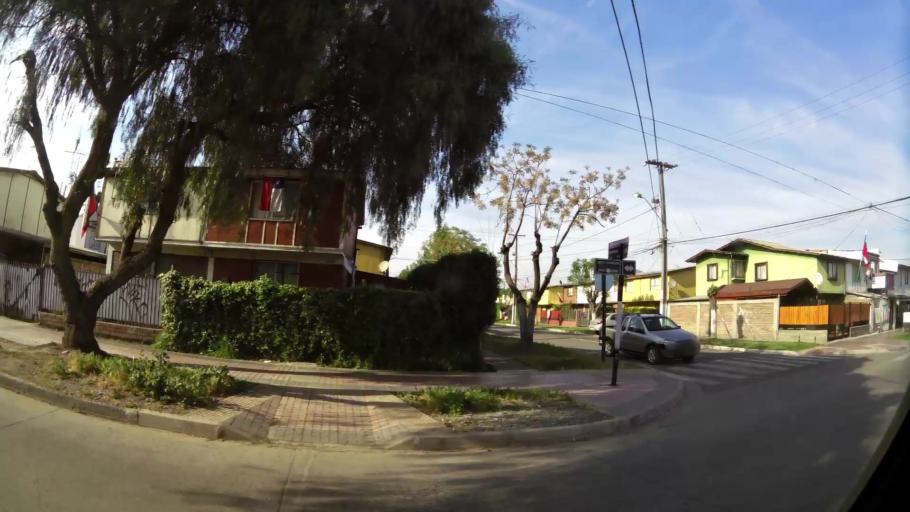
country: CL
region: Santiago Metropolitan
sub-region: Provincia de Talagante
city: Talagante
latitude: -33.6726
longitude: -70.9388
